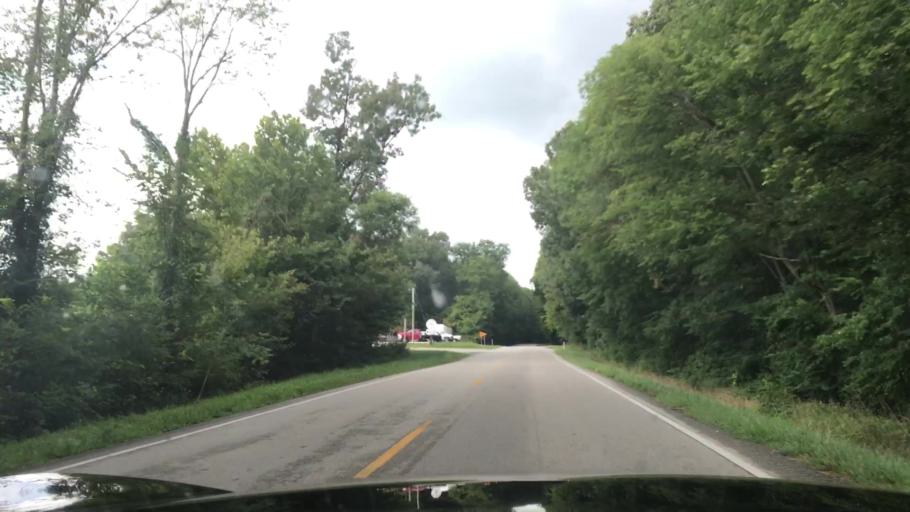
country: US
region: Kentucky
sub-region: Butler County
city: Morgantown
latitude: 37.1829
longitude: -86.7761
